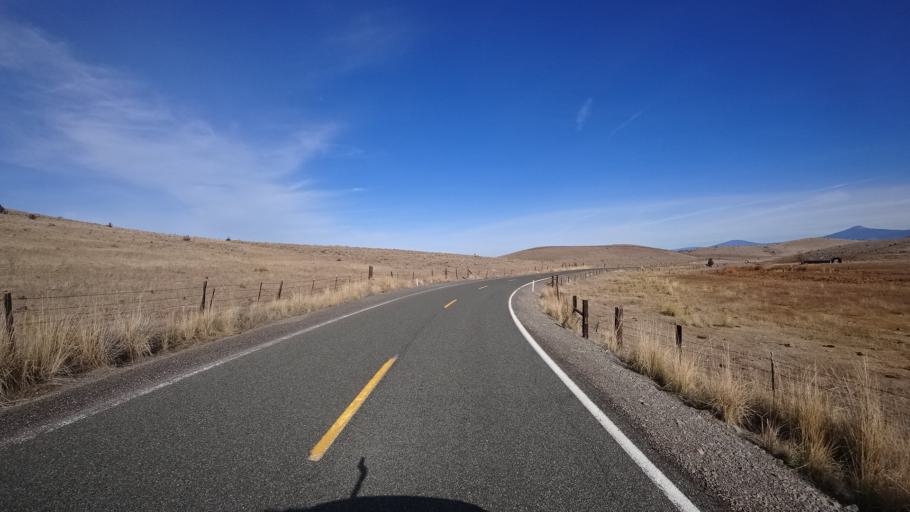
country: US
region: California
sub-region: Siskiyou County
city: Weed
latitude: 41.5456
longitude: -122.4994
